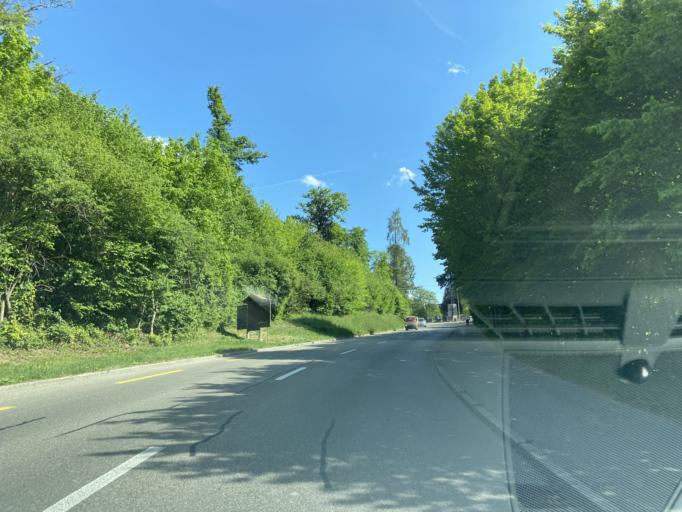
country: CH
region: Zurich
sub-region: Bezirk Buelach
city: Rorbas
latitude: 47.5249
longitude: 8.5802
